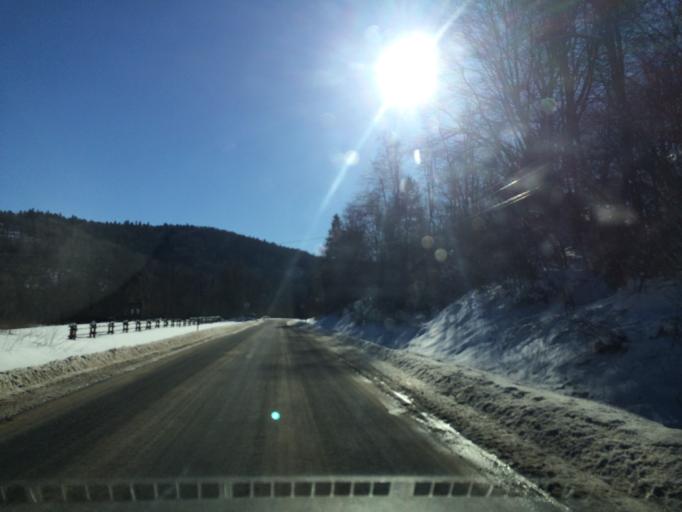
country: PL
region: Subcarpathian Voivodeship
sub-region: Powiat bieszczadzki
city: Lutowiska
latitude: 49.1704
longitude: 22.6887
